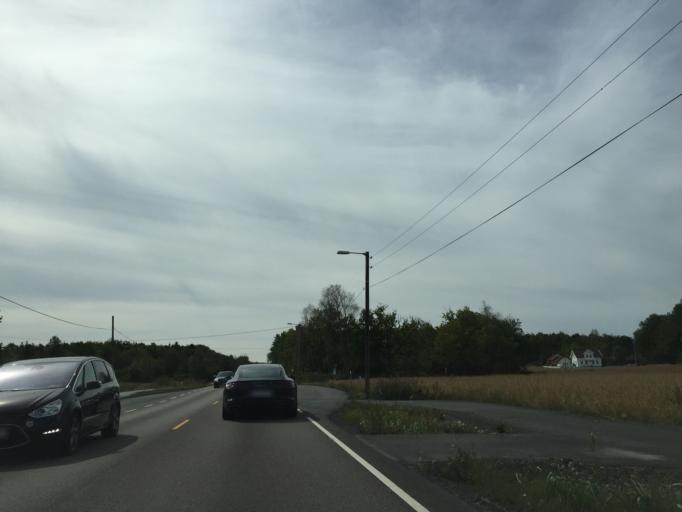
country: NO
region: Ostfold
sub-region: Fredrikstad
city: Fredrikstad
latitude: 59.1687
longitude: 10.9311
